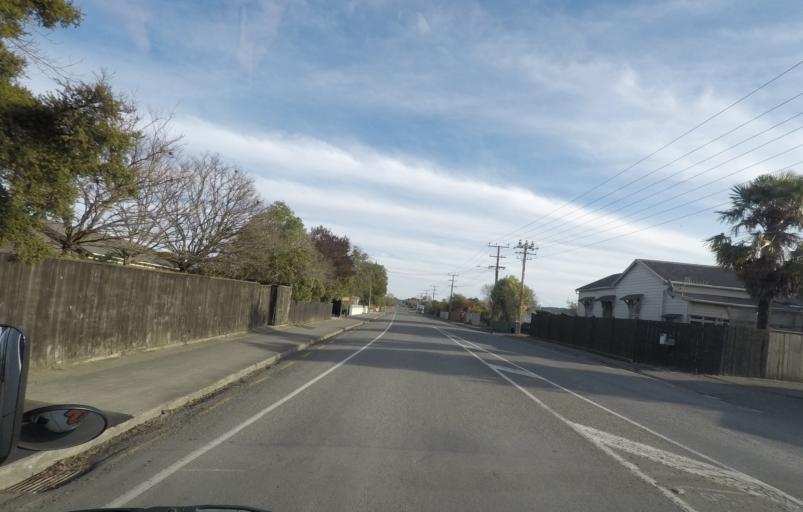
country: NZ
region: Tasman
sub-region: Tasman District
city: Brightwater
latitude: -41.3740
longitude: 173.1071
